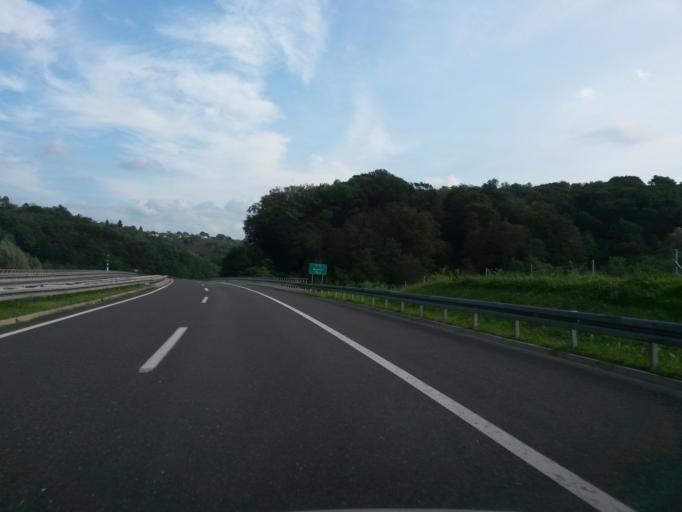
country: HR
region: Varazdinska
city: Jalzabet
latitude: 46.2429
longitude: 16.4040
